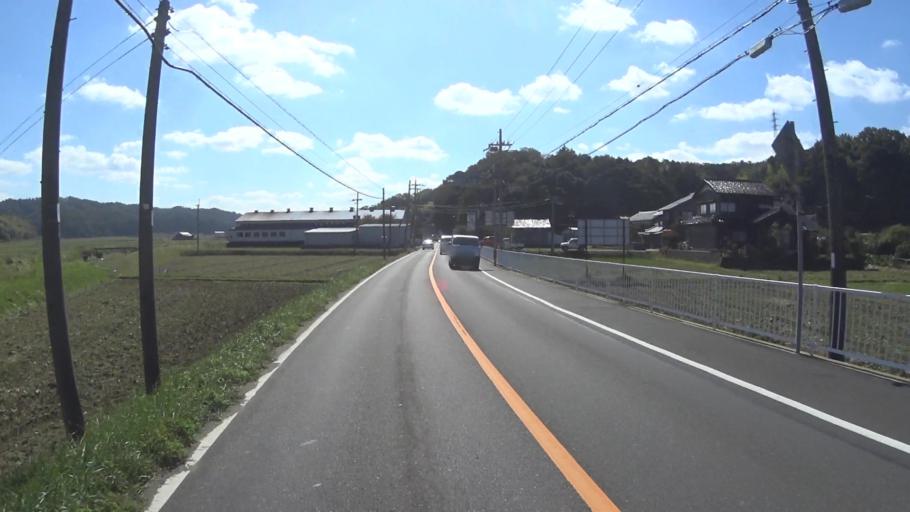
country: JP
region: Kyoto
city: Miyazu
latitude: 35.6679
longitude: 135.0277
